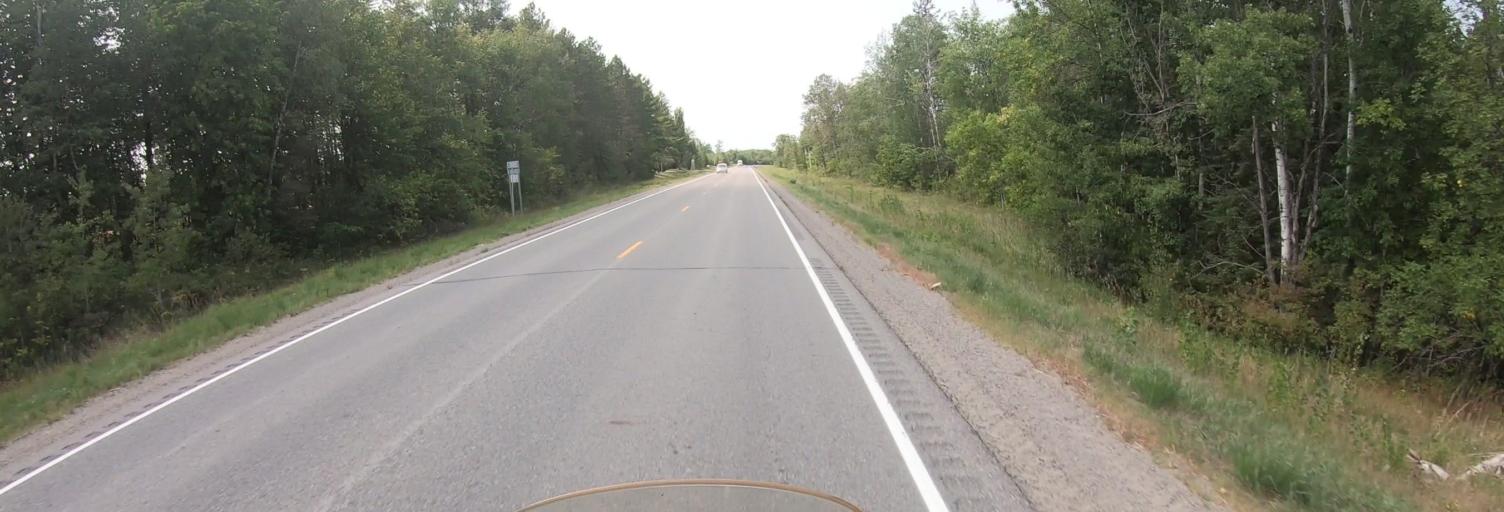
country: US
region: Minnesota
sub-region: Lake of the Woods County
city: Baudette
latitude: 48.6437
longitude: -94.1468
